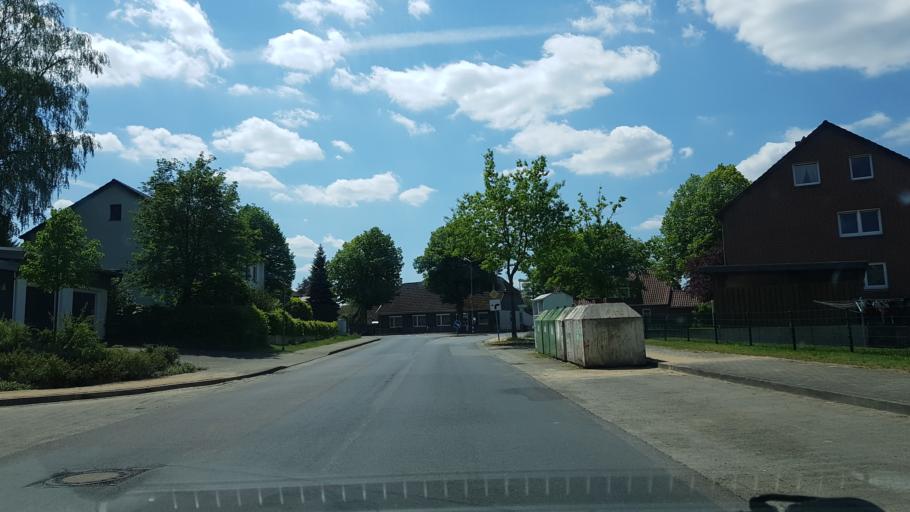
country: DE
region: Lower Saxony
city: Eschede
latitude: 52.7392
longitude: 10.2324
